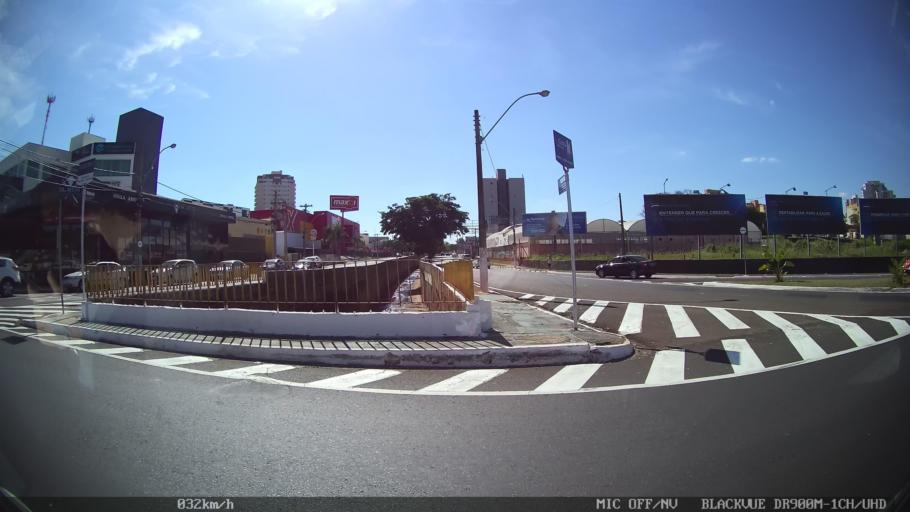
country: BR
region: Sao Paulo
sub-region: Franca
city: Franca
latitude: -20.5522
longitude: -47.4095
